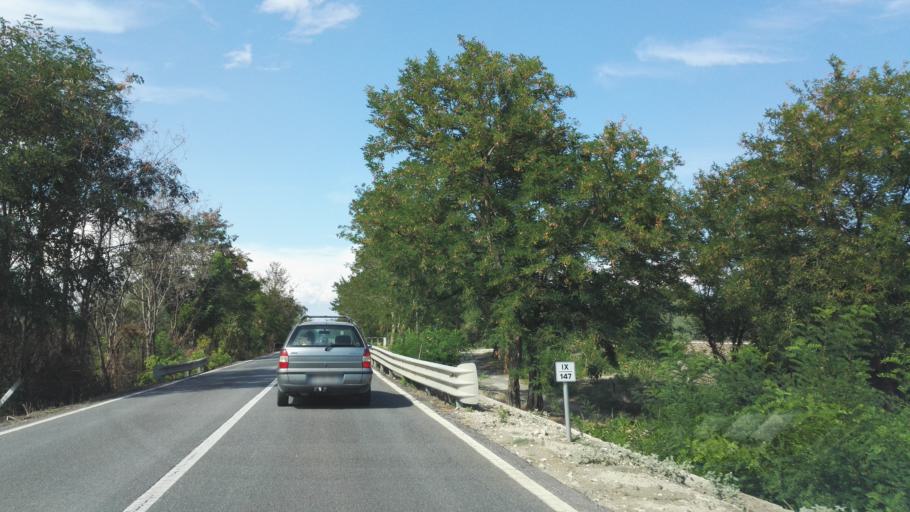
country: IT
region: Calabria
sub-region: Provincia di Catanzaro
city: Santa Caterina dello Ionio Marina
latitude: 38.5470
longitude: 16.5700
